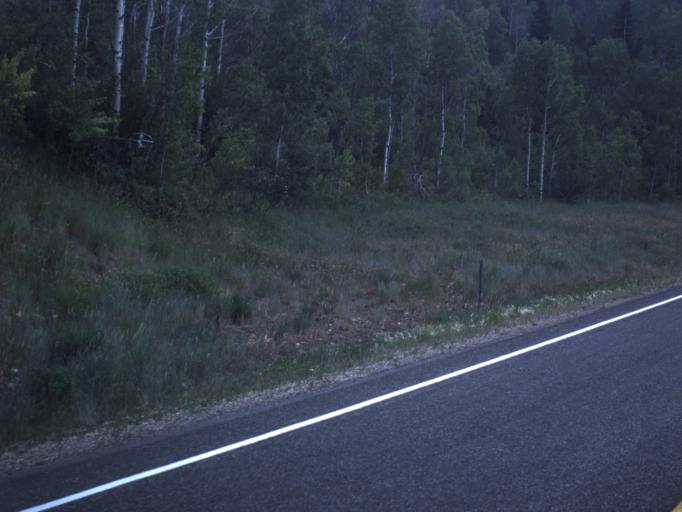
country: US
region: Utah
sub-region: Summit County
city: Francis
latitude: 40.5353
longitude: -111.0989
